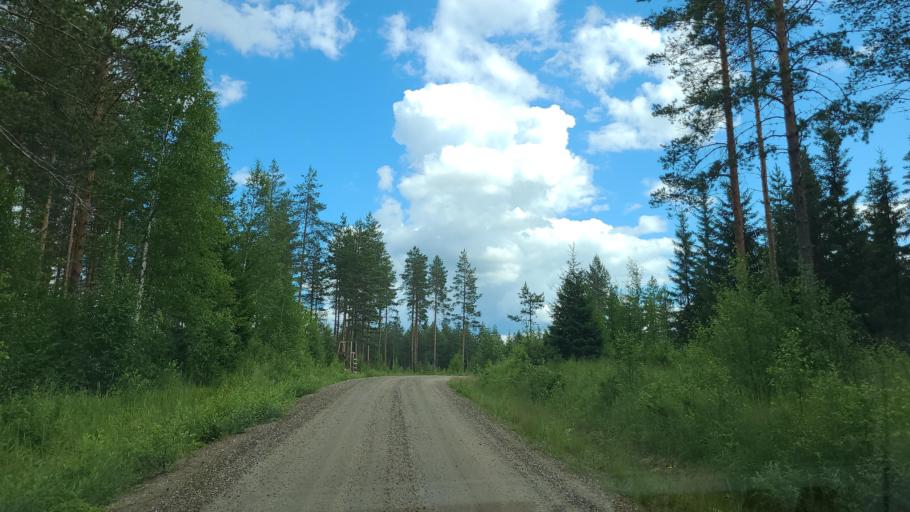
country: FI
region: Northern Savo
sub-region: Koillis-Savo
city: Kaavi
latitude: 63.0343
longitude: 28.7850
